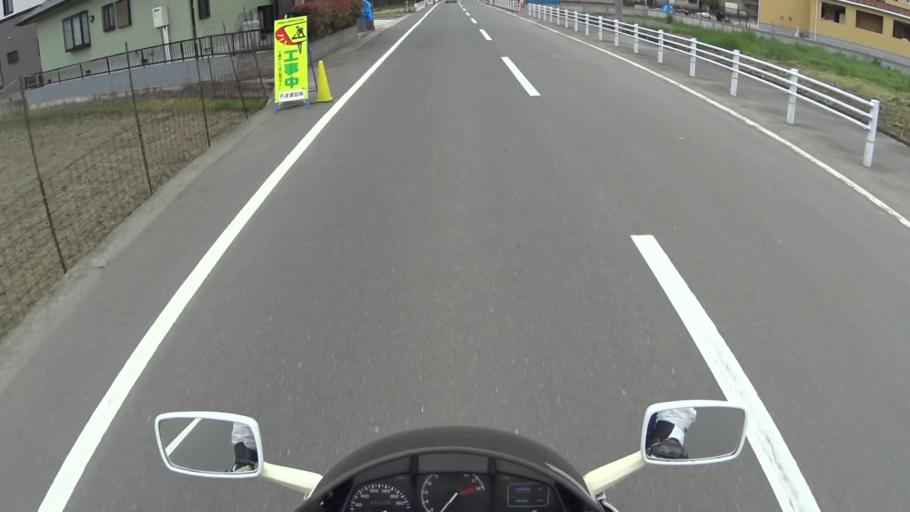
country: JP
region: Kyoto
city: Kameoka
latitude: 35.0663
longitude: 135.5333
